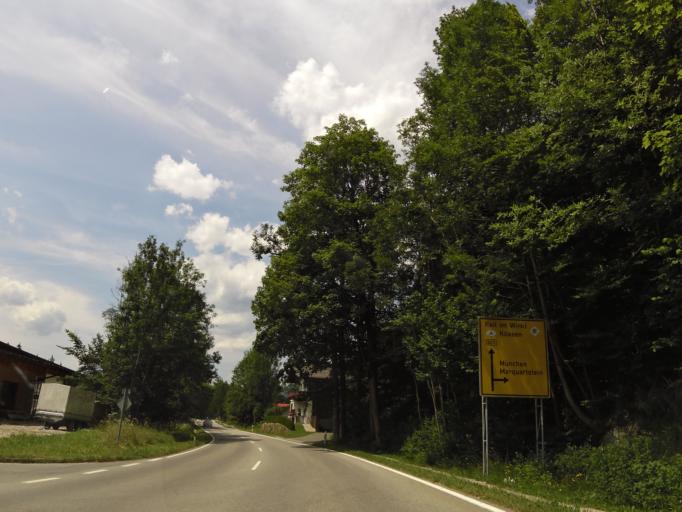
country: DE
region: Bavaria
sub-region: Upper Bavaria
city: Reit im Winkl
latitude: 47.6709
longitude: 12.4905
